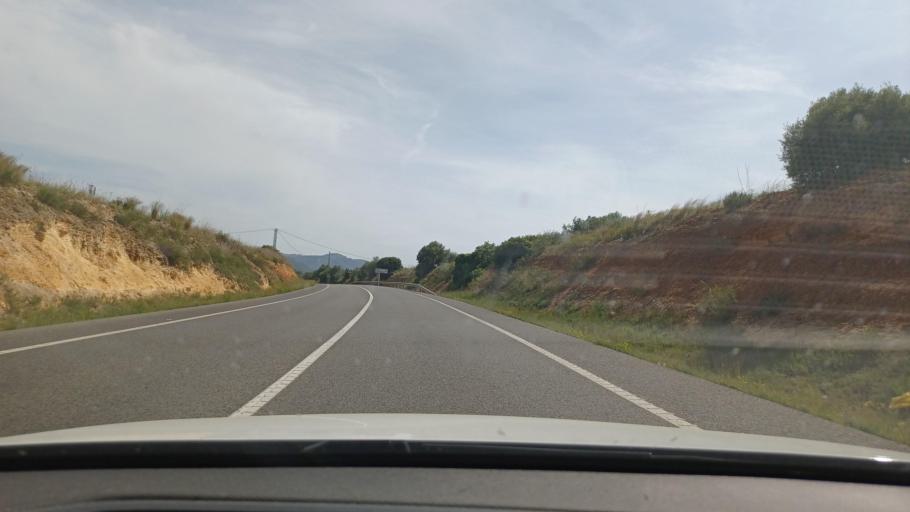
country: ES
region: Catalonia
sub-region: Provincia de Tarragona
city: Amposta
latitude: 40.7199
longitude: 0.5636
